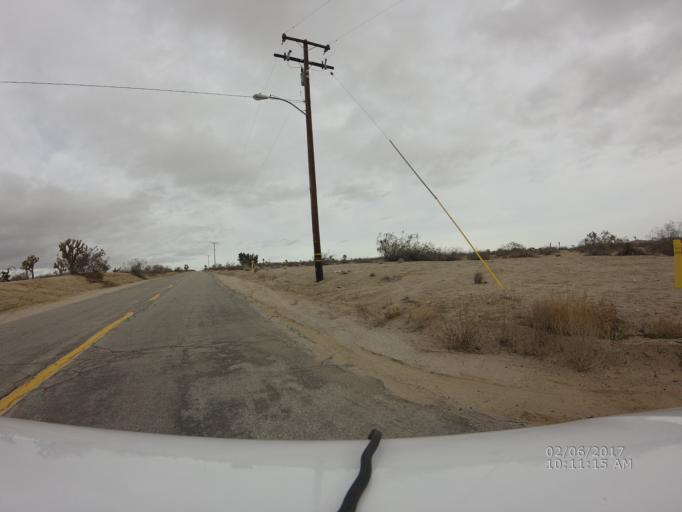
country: US
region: California
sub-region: Los Angeles County
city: Lake Los Angeles
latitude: 34.6907
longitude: -117.7740
